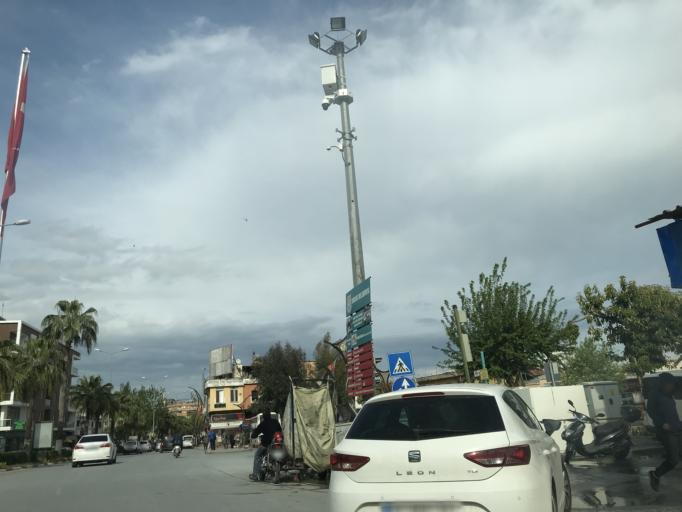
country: TR
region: Mersin
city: Tarsus
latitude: 36.9165
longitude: 34.8952
